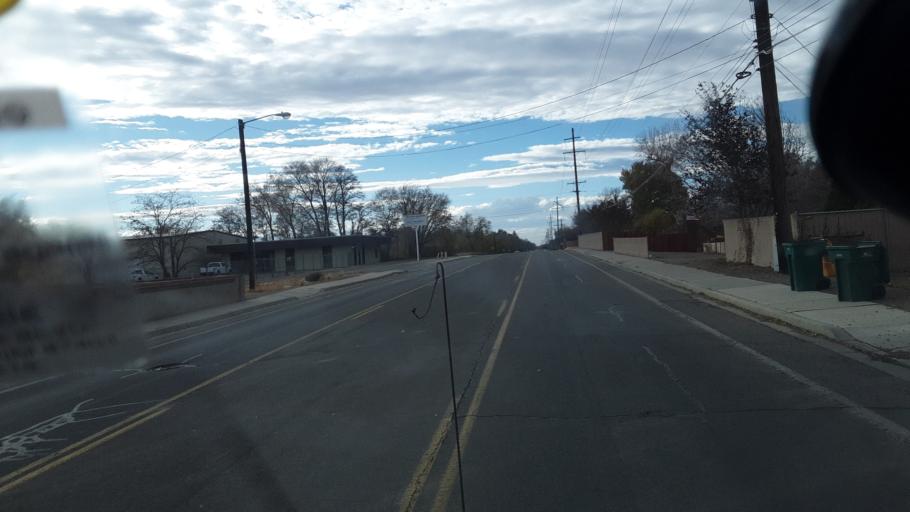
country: US
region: New Mexico
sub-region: San Juan County
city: Farmington
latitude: 36.7265
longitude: -108.1715
